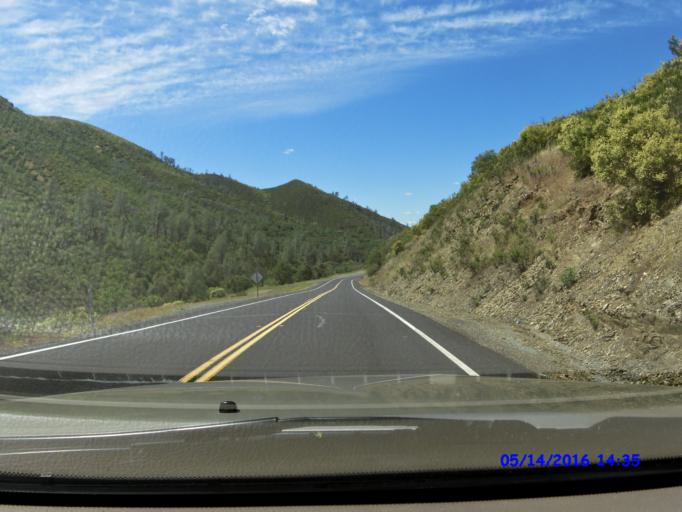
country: US
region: California
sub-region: Tuolumne County
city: Tuolumne City
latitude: 37.7761
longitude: -120.2691
